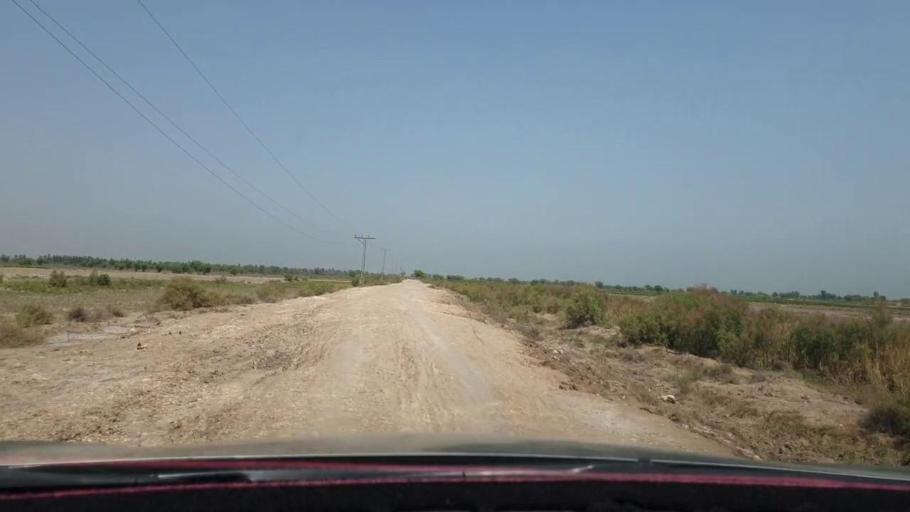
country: PK
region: Sindh
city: Warah
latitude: 27.3959
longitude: 67.6864
